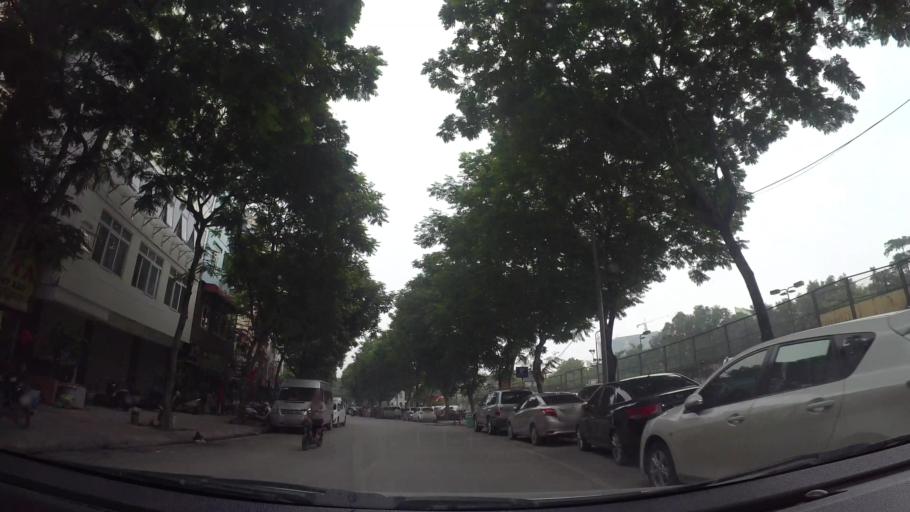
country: VN
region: Ha Noi
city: Cau Giay
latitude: 21.0331
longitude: 105.8172
